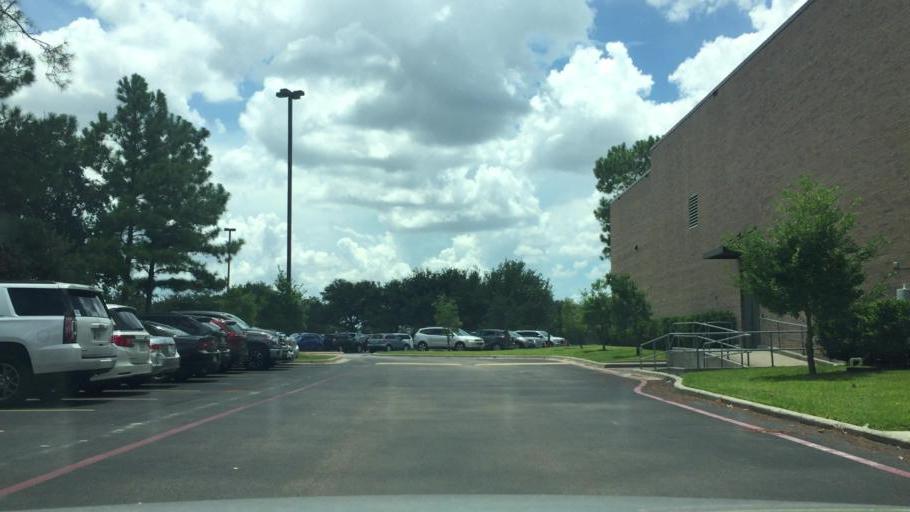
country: US
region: Texas
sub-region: Harris County
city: Hudson
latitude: 29.8494
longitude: -95.4979
